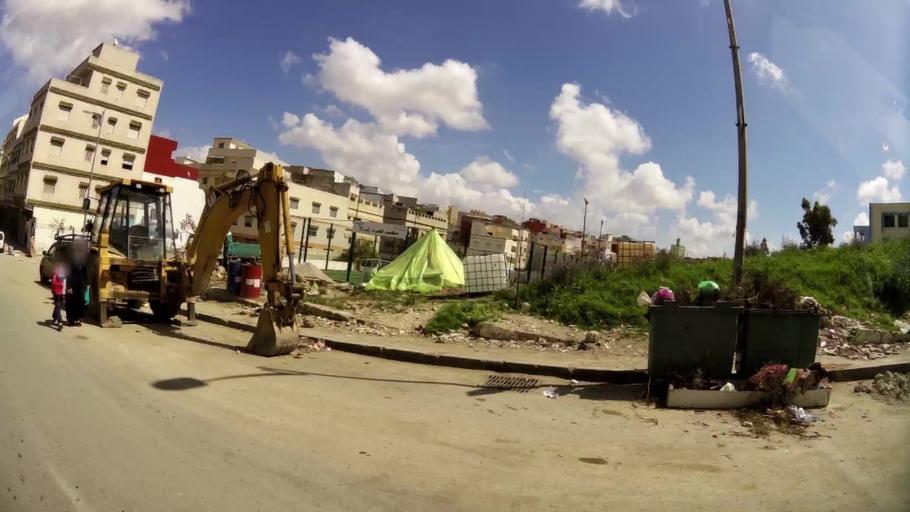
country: MA
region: Tanger-Tetouan
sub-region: Tanger-Assilah
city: Tangier
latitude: 35.7572
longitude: -5.8243
